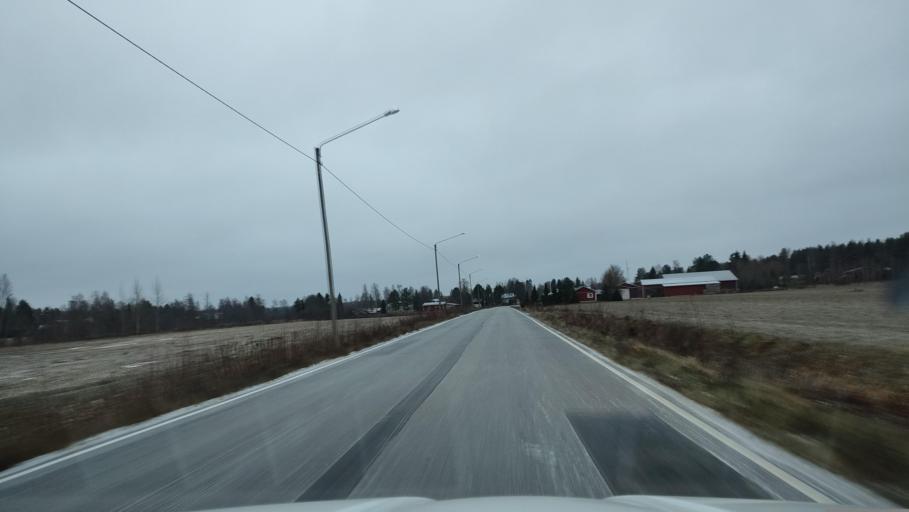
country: FI
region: Southern Ostrobothnia
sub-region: Suupohja
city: Karijoki
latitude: 62.2360
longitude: 21.6537
